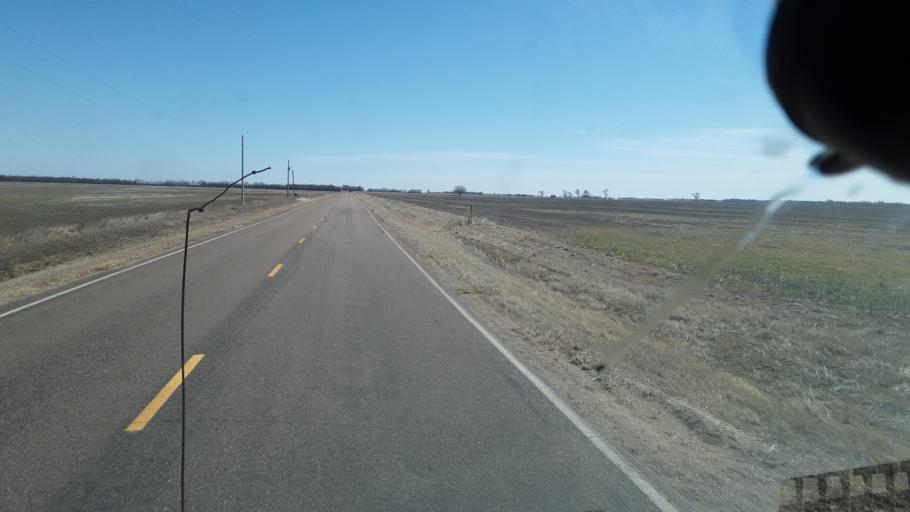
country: US
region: Kansas
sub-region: Rice County
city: Sterling
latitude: 38.2461
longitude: -98.2525
